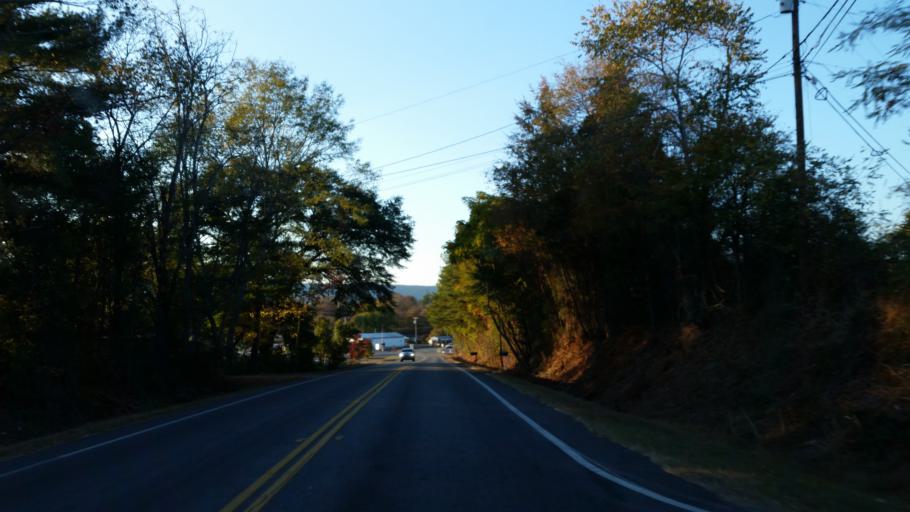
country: US
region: Georgia
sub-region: Gordon County
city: Calhoun
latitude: 34.5556
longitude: -85.0097
